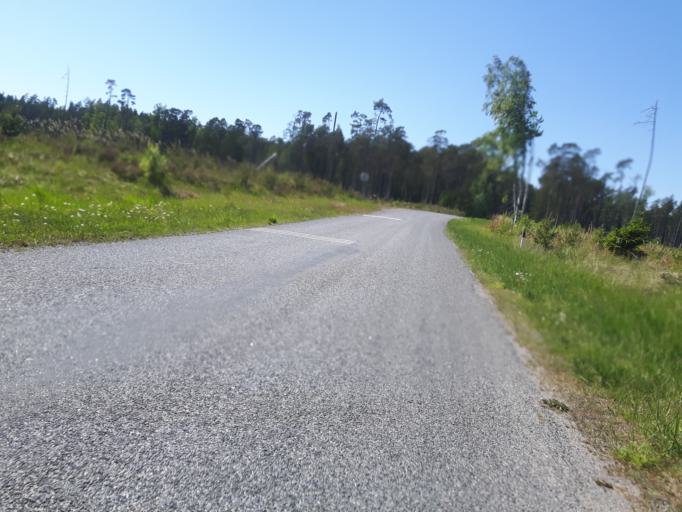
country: EE
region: Laeaene-Virumaa
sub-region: Haljala vald
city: Haljala
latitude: 59.5711
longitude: 26.2884
